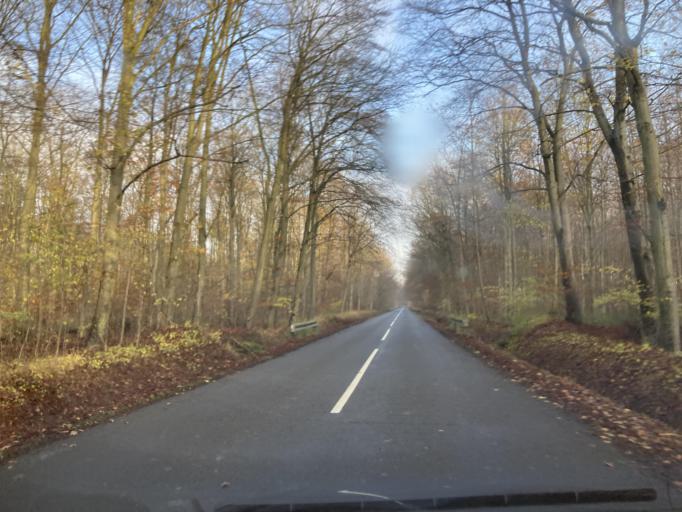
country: DK
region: Zealand
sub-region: Lolland Kommune
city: Rodby
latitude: 54.7680
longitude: 11.3615
